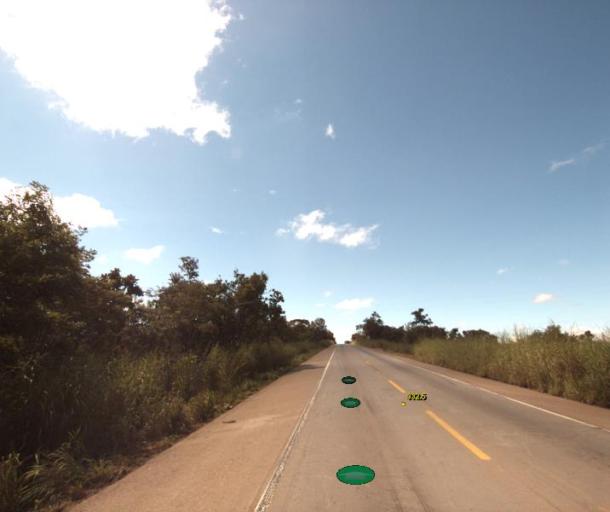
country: BR
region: Goias
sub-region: Uruana
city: Uruana
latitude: -15.5328
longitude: -49.4494
